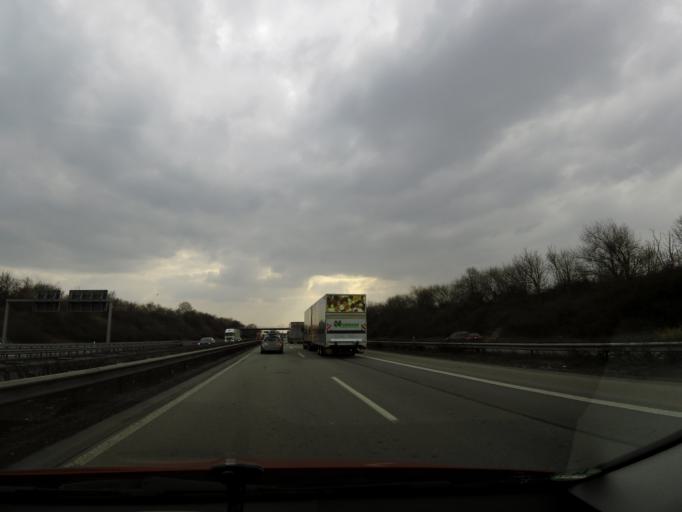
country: DE
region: Rheinland-Pfalz
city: Kleinniedesheim
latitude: 49.6220
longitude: 8.2937
